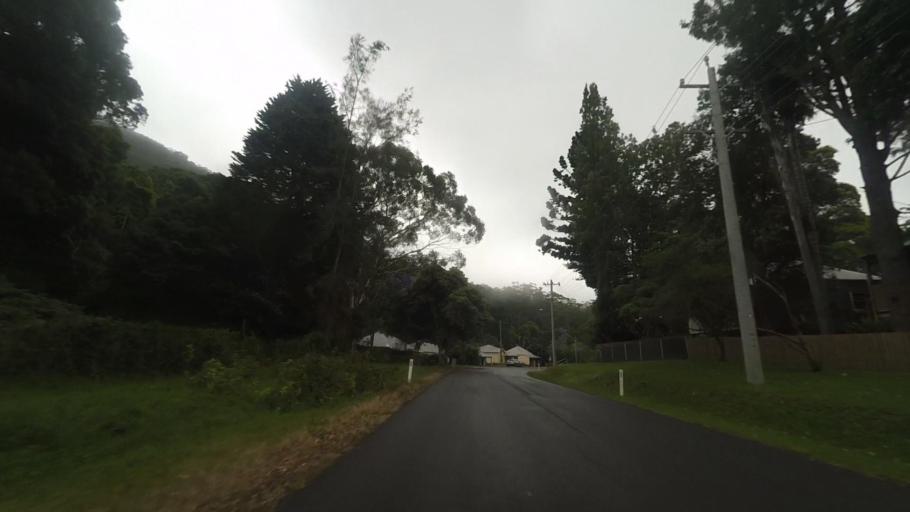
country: AU
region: New South Wales
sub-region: Wollongong
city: Cordeaux Heights
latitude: -34.4309
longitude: 150.8064
